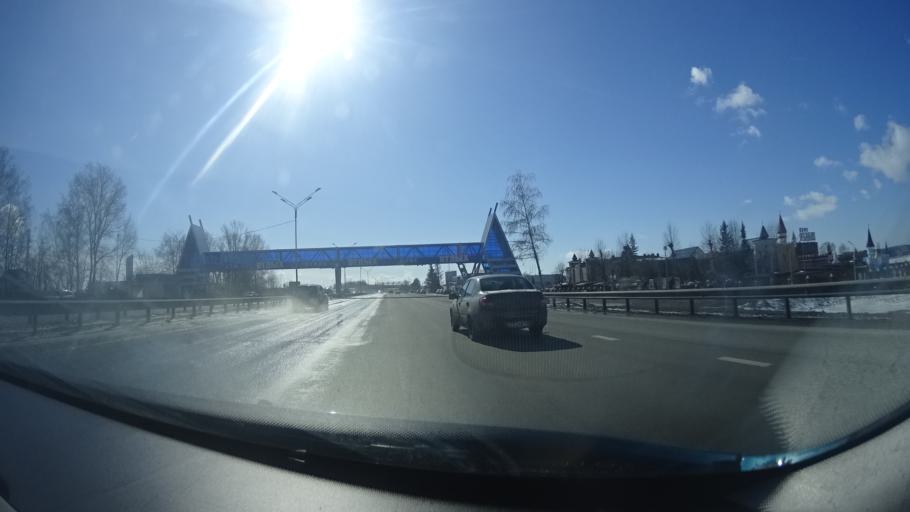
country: RU
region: Bashkortostan
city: Ufa
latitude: 54.6390
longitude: 55.9304
